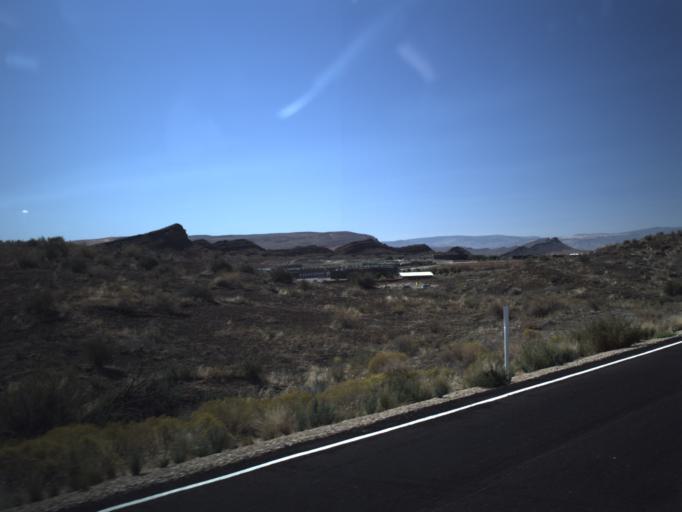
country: US
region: Utah
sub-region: Washington County
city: Washington
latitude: 37.1717
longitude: -113.4048
